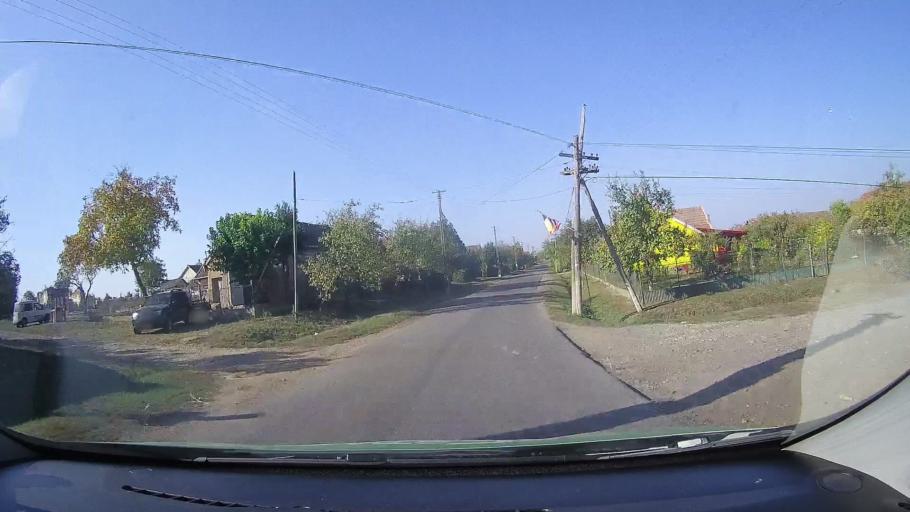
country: RO
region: Satu Mare
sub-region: Comuna Sauca
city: Sauca
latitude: 47.4716
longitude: 22.5194
